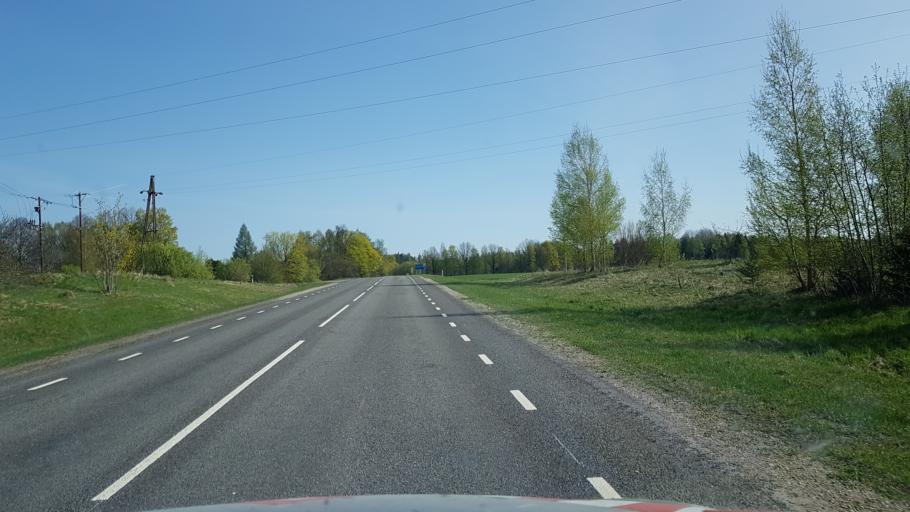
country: EE
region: Viljandimaa
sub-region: Viljandi linn
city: Viljandi
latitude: 58.2378
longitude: 25.5887
